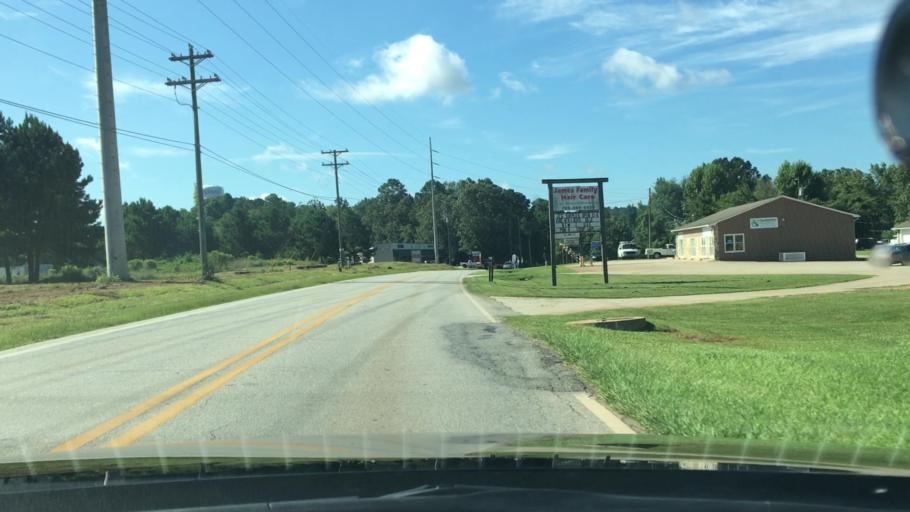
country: US
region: Georgia
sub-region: Putnam County
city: Jefferson
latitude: 33.4196
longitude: -83.2675
